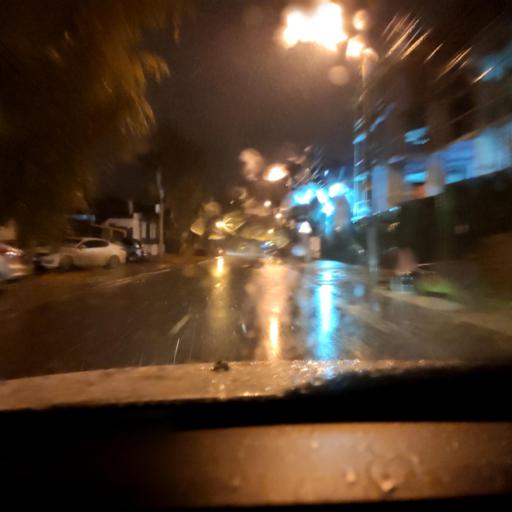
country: RU
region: Voronezj
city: Voronezh
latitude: 51.6537
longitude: 39.2013
